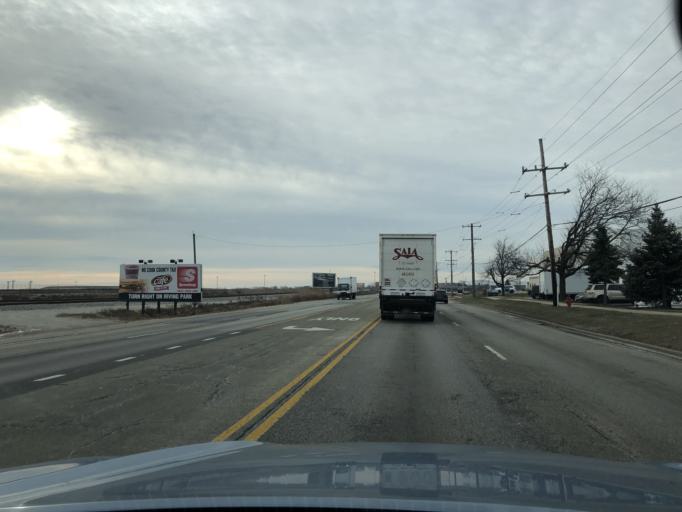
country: US
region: Illinois
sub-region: DuPage County
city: Bensenville
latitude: 41.9688
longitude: -87.9398
